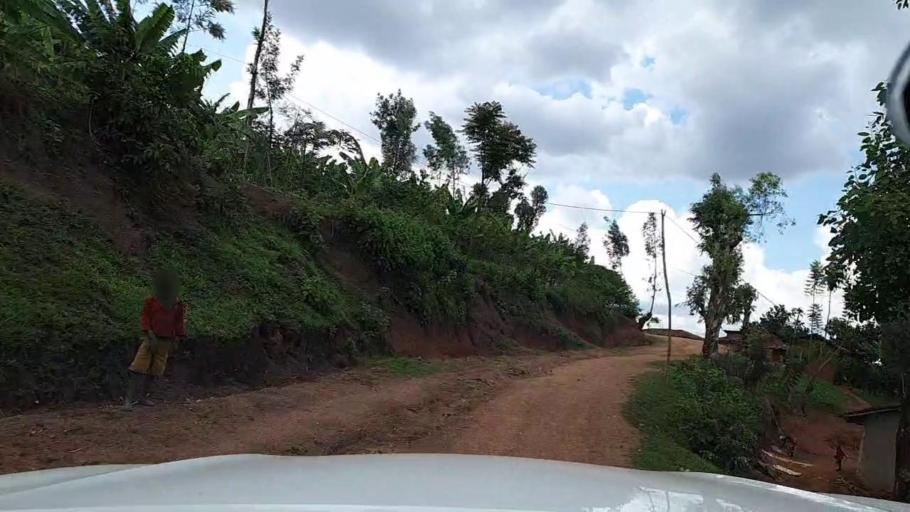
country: RW
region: Southern Province
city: Butare
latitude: -2.7522
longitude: 29.7595
